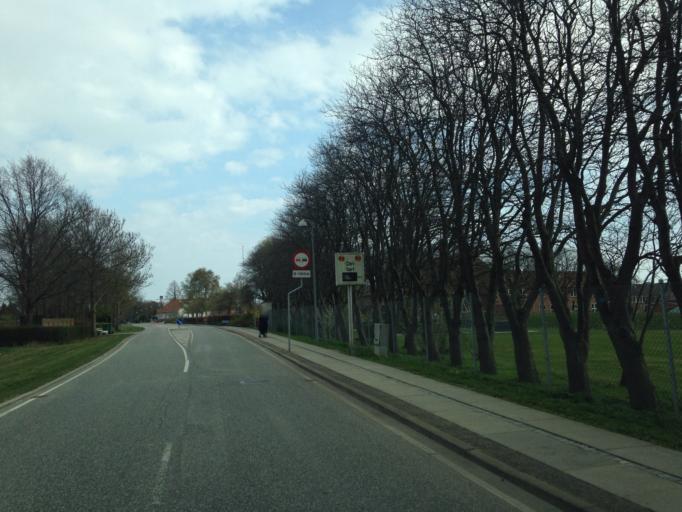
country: DK
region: Capital Region
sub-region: Hoje-Taastrup Kommune
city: Taastrup
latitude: 55.6266
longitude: 12.2953
